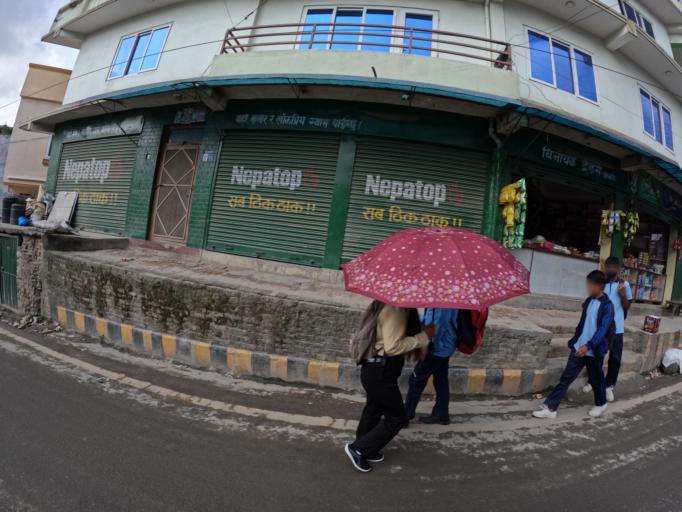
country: NP
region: Central Region
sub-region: Bagmati Zone
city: Patan
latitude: 27.6679
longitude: 85.3656
